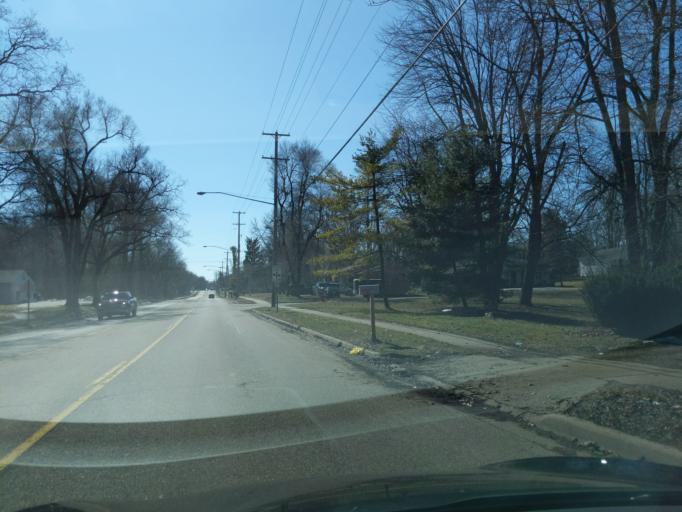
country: US
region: Michigan
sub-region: Ingham County
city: Holt
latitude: 42.6744
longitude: -84.5629
